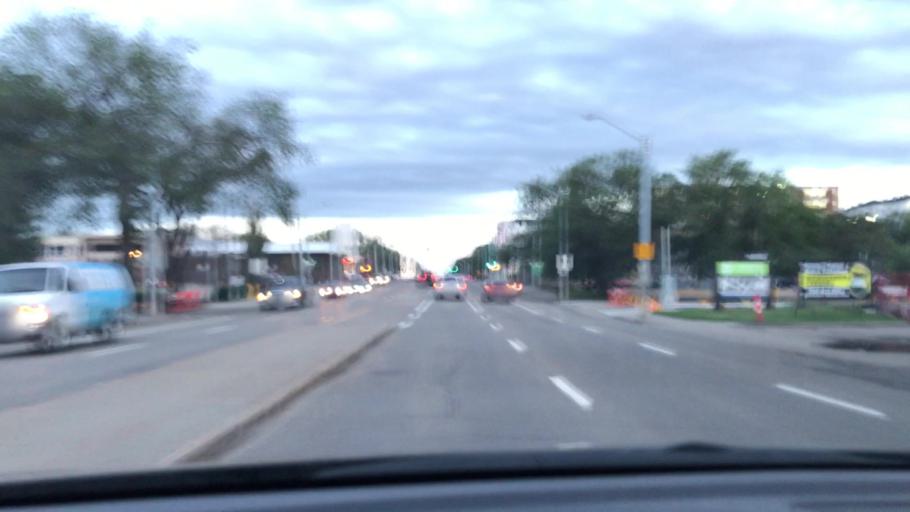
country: CA
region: Alberta
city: Edmonton
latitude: 53.5196
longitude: -113.5121
